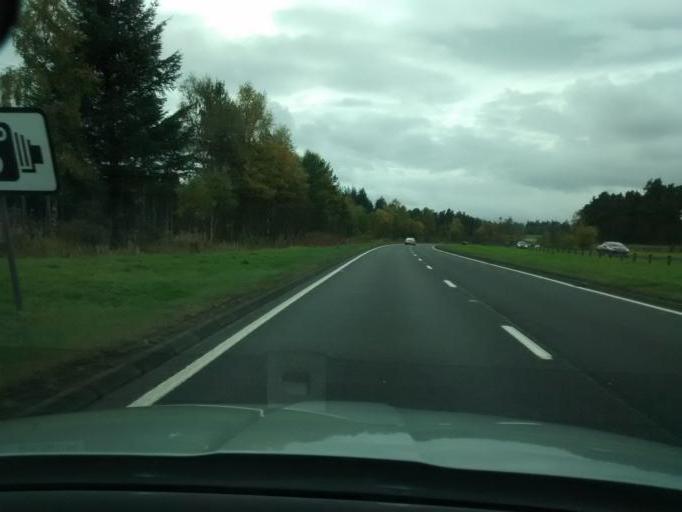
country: GB
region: Scotland
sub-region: Perth and Kinross
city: Perth
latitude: 56.3823
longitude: -3.5081
